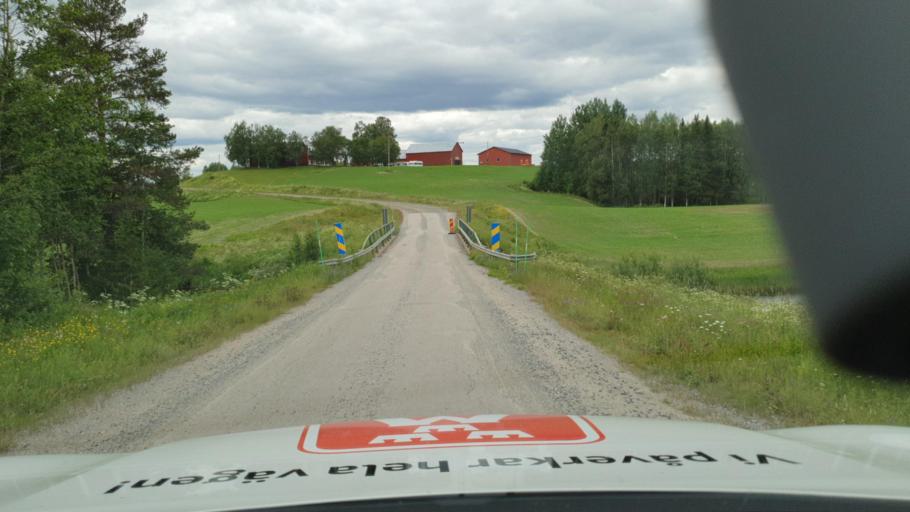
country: SE
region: Vaesterbotten
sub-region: Bjurholms Kommun
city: Bjurholm
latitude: 63.7551
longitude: 19.2711
